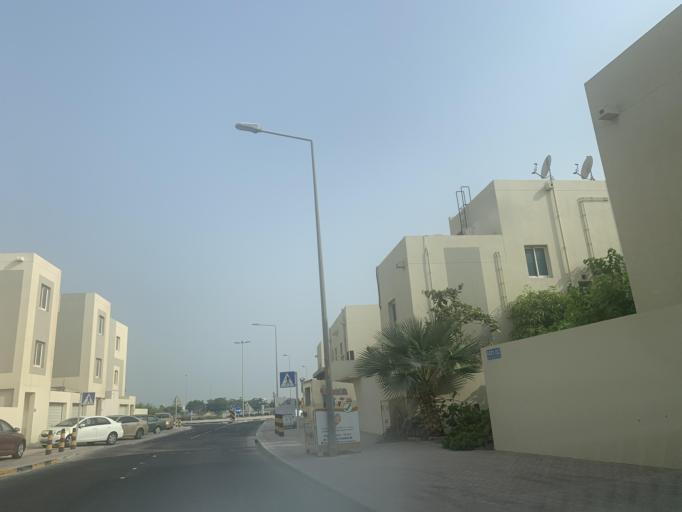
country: BH
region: Manama
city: Jidd Hafs
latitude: 26.2279
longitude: 50.4536
